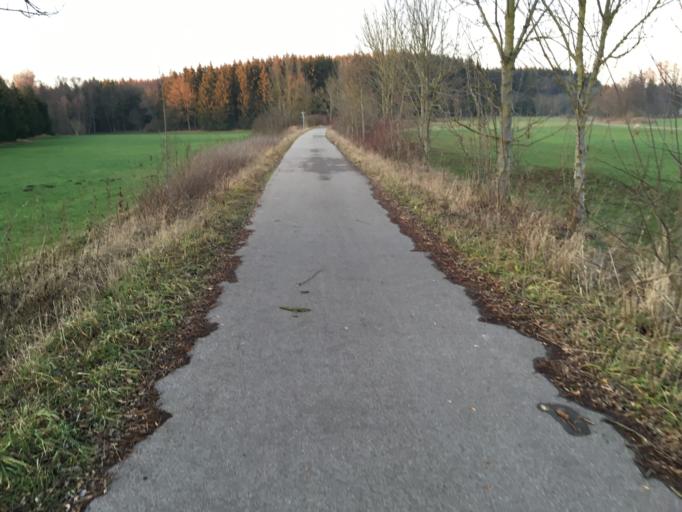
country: DE
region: Bavaria
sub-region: Swabia
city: Hawangen
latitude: 47.9745
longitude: 10.2827
